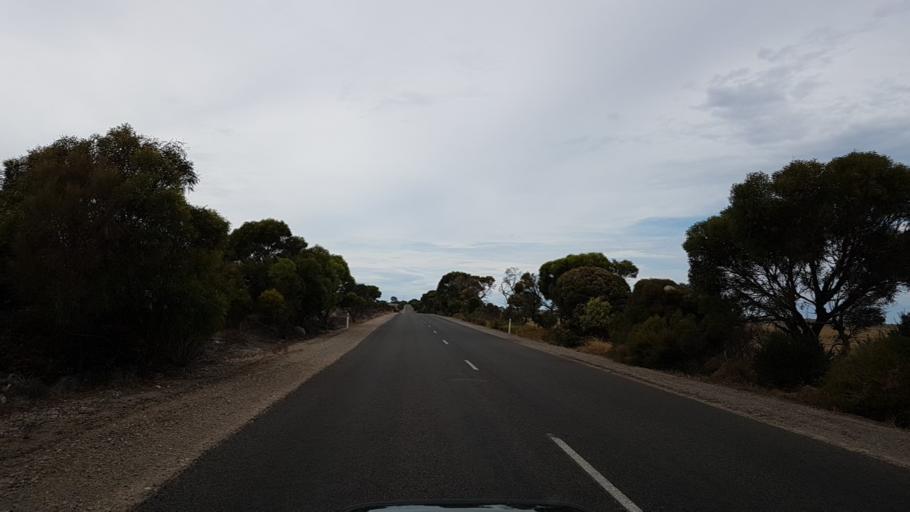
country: AU
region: South Australia
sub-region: Yorke Peninsula
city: Honiton
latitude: -34.9769
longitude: 137.1168
